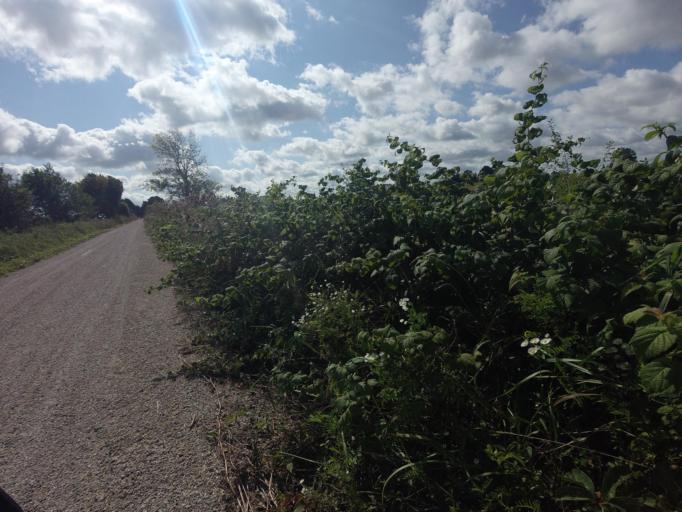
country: CA
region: Ontario
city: Huron East
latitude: 43.7175
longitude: -81.3903
